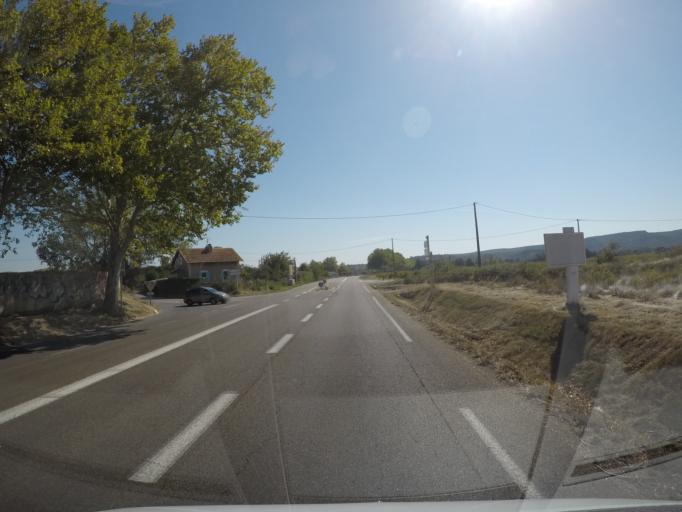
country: FR
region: Languedoc-Roussillon
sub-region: Departement du Gard
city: Castillon-du-Gard
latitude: 43.9663
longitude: 4.5089
